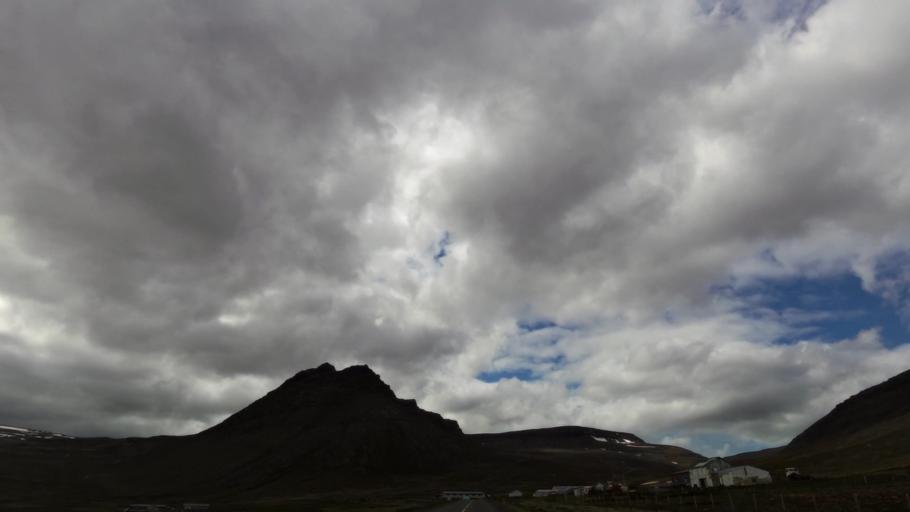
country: IS
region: Westfjords
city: Isafjoerdur
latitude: 66.1587
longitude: -23.2757
